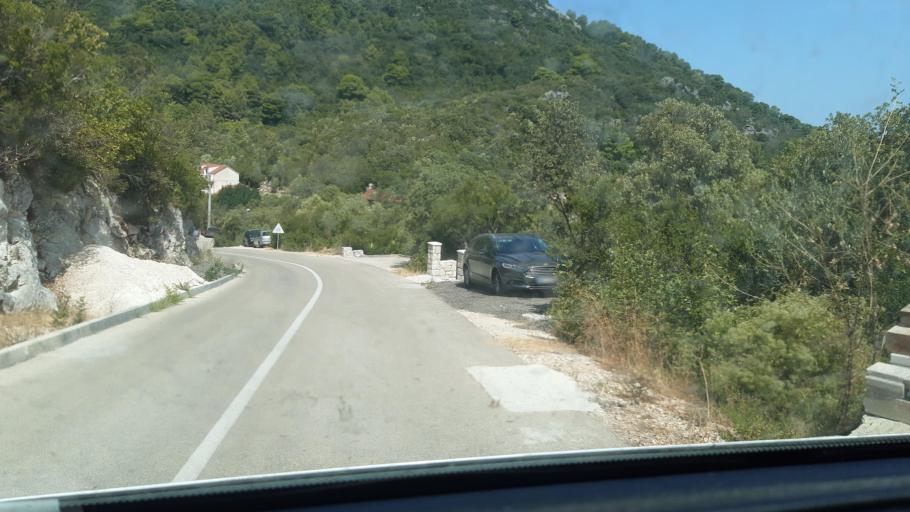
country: HR
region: Dubrovacko-Neretvanska
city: Ston
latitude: 42.7252
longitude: 17.6684
